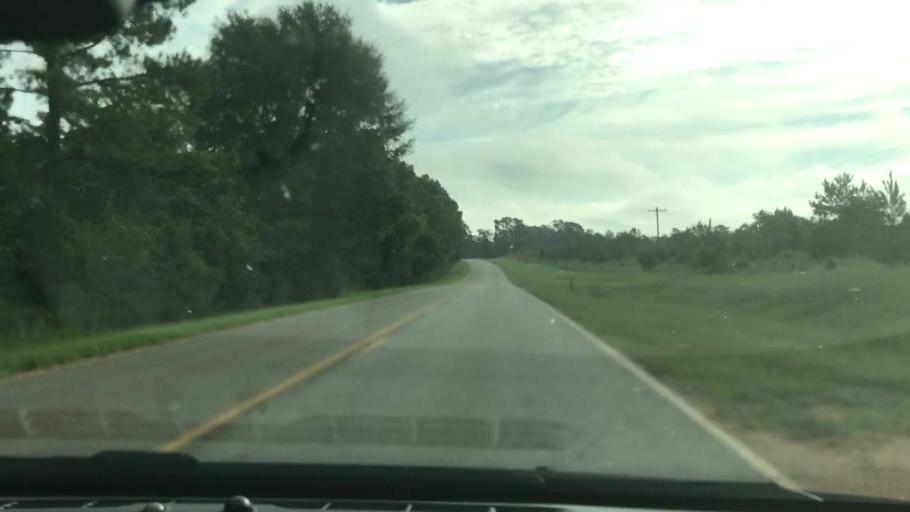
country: US
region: Georgia
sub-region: Quitman County
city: Georgetown
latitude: 31.9010
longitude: -85.0450
